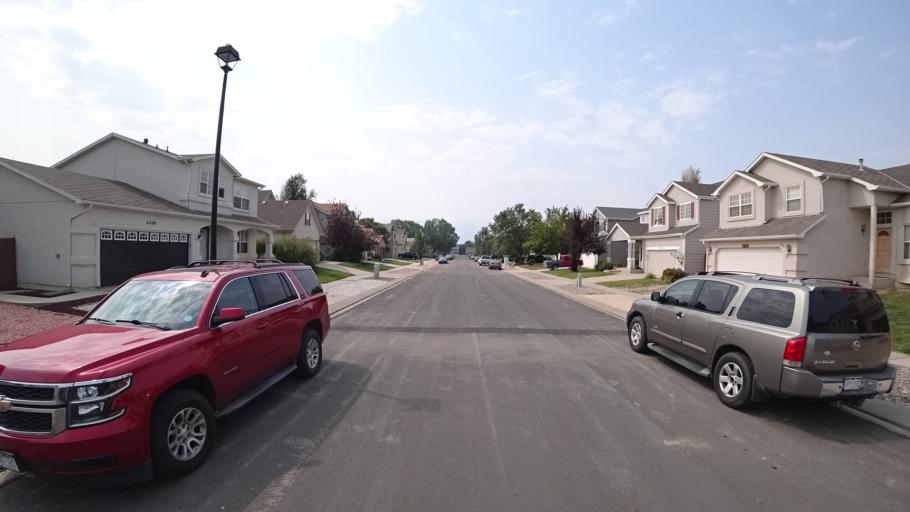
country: US
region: Colorado
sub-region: El Paso County
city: Cimarron Hills
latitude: 38.8281
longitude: -104.7407
